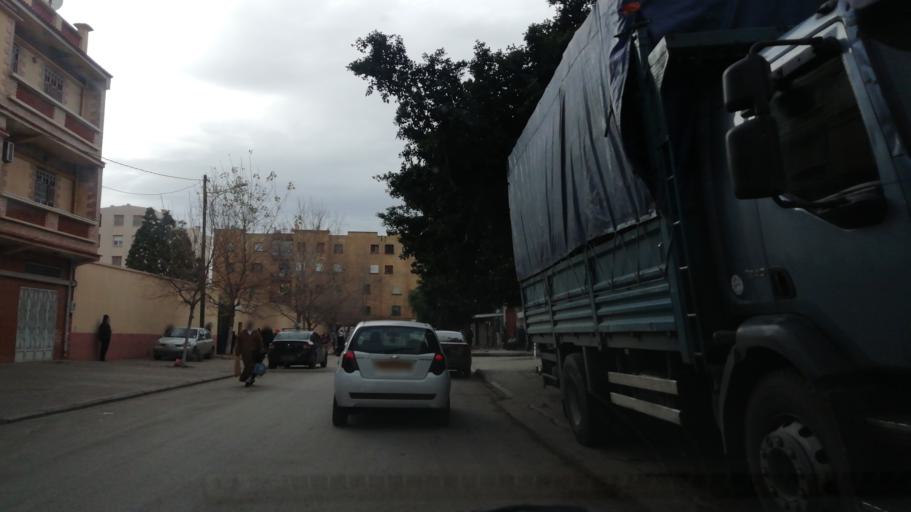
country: DZ
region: Oran
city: Oran
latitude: 35.6844
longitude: -0.5973
